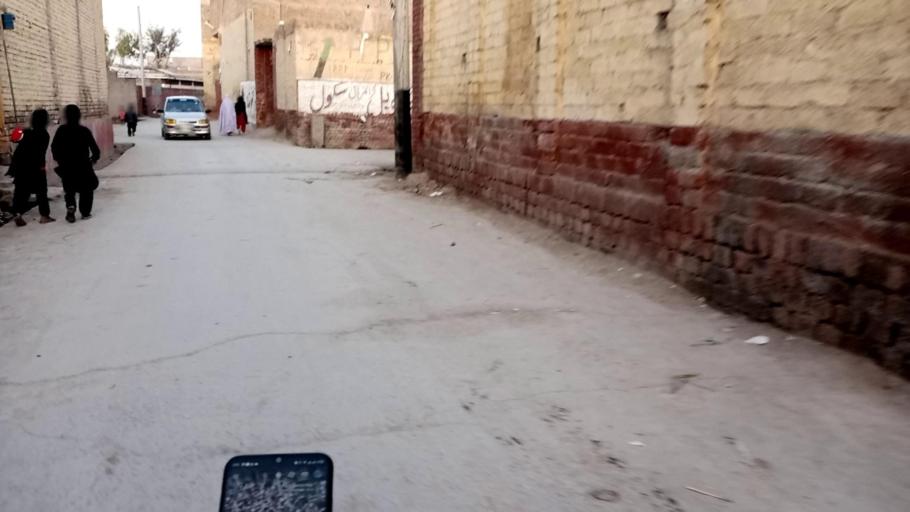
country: PK
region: Khyber Pakhtunkhwa
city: Peshawar
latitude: 34.0511
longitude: 71.4605
